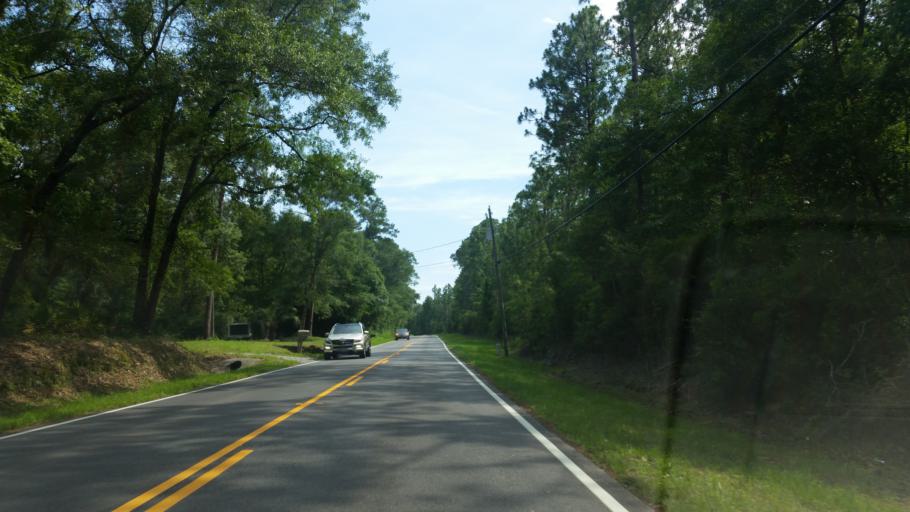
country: US
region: Florida
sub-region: Escambia County
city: Cantonment
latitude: 30.5866
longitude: -87.3967
